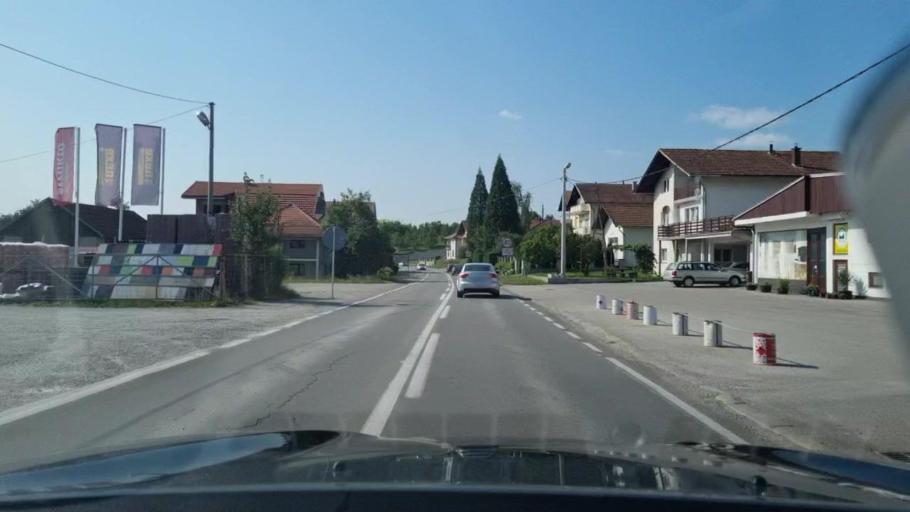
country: BA
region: Federation of Bosnia and Herzegovina
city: Coralici
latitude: 44.9778
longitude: 15.8935
